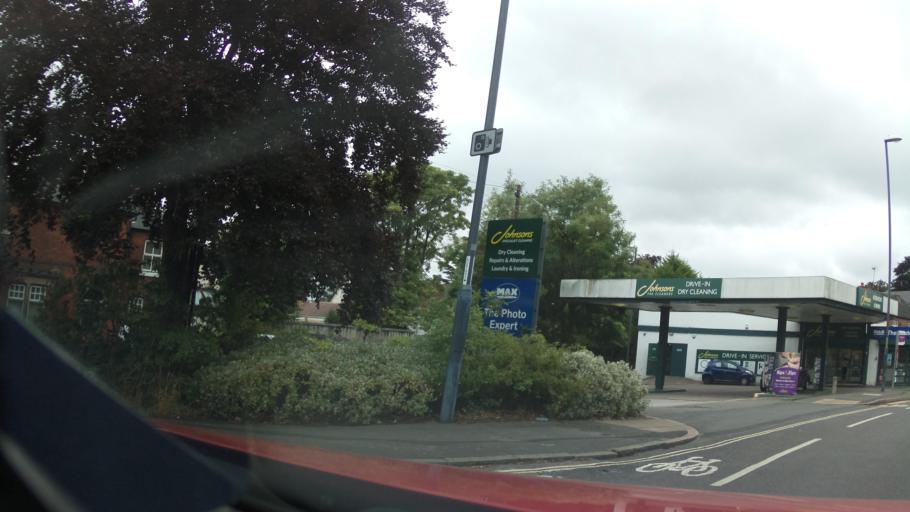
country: GB
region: England
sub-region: Derby
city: Derby
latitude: 52.9115
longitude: -1.4890
